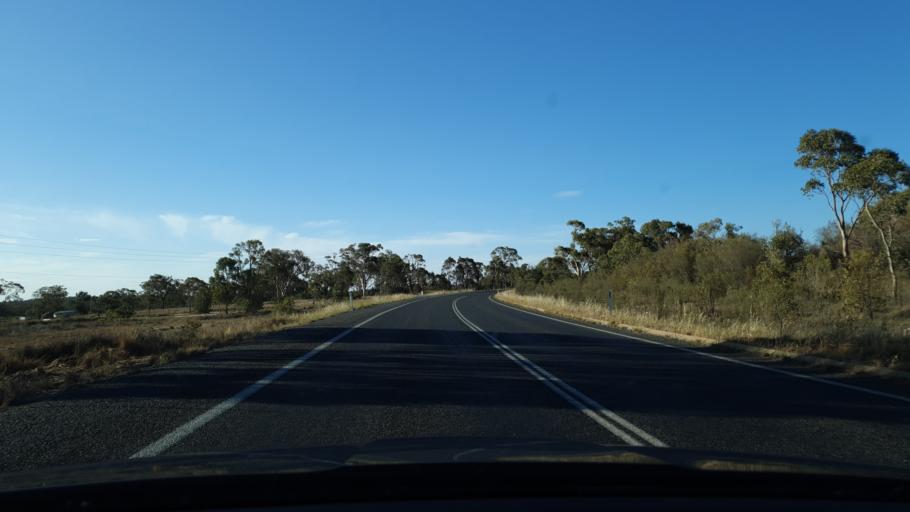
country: AU
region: Queensland
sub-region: Southern Downs
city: Stanthorpe
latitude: -28.6693
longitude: 151.9163
